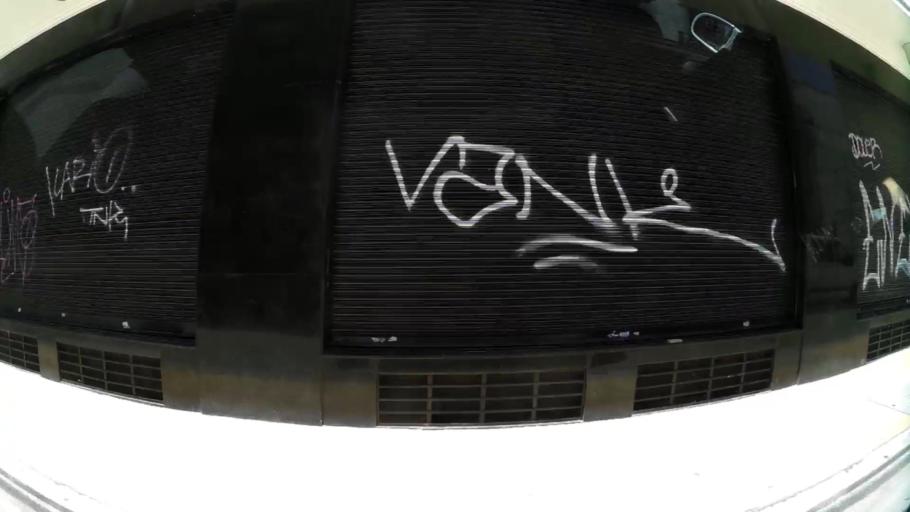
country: AR
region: Buenos Aires F.D.
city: Buenos Aires
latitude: -34.6137
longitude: -58.3737
